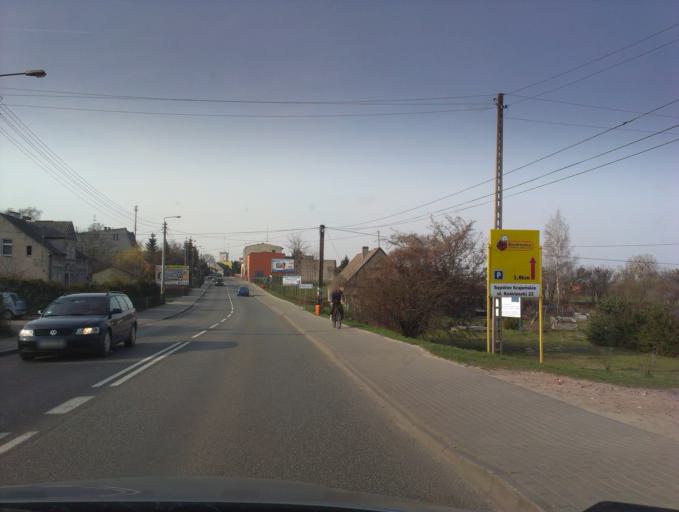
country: PL
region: Kujawsko-Pomorskie
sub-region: Powiat sepolenski
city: Sepolno Krajenskie
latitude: 53.4442
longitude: 17.5303
